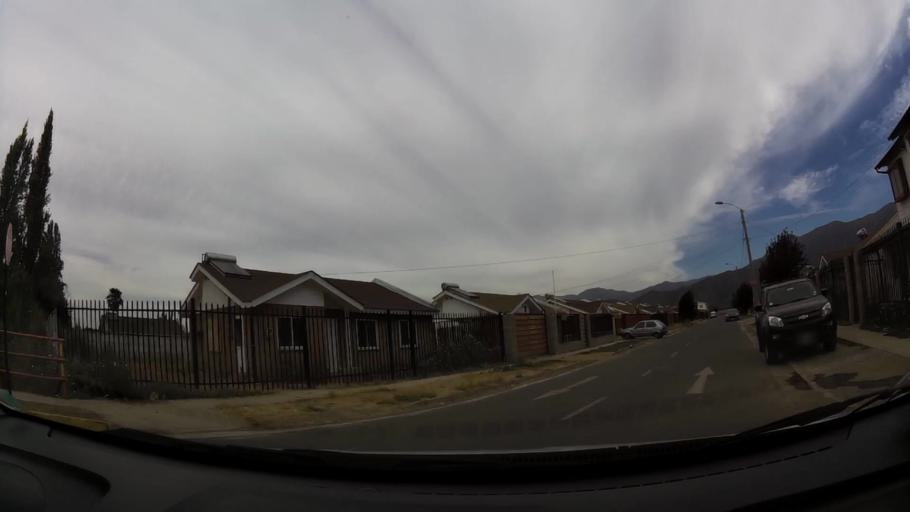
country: CL
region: O'Higgins
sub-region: Provincia de Cachapoal
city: Graneros
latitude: -34.0803
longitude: -70.7359
